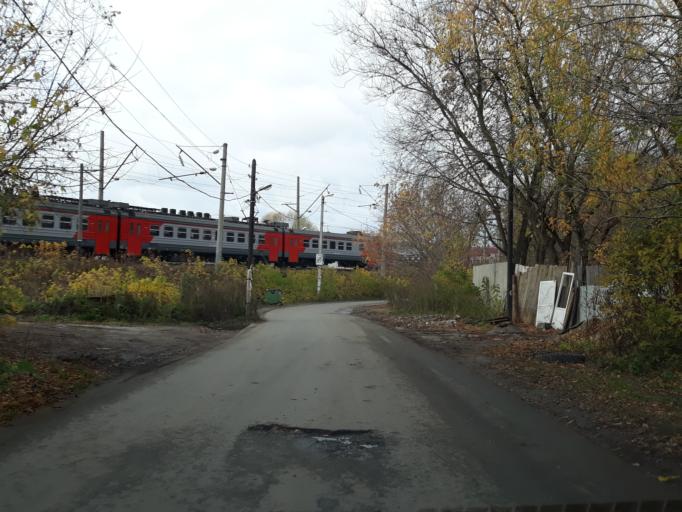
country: RU
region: Nizjnij Novgorod
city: Nizhniy Novgorod
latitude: 56.2543
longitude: 43.9733
